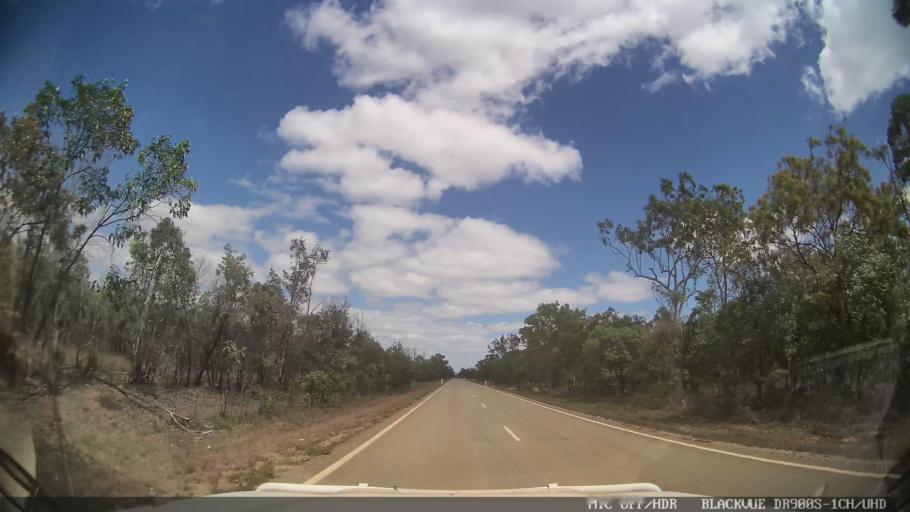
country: AU
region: Queensland
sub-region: Tablelands
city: Ravenshoe
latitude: -17.8144
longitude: 144.9567
